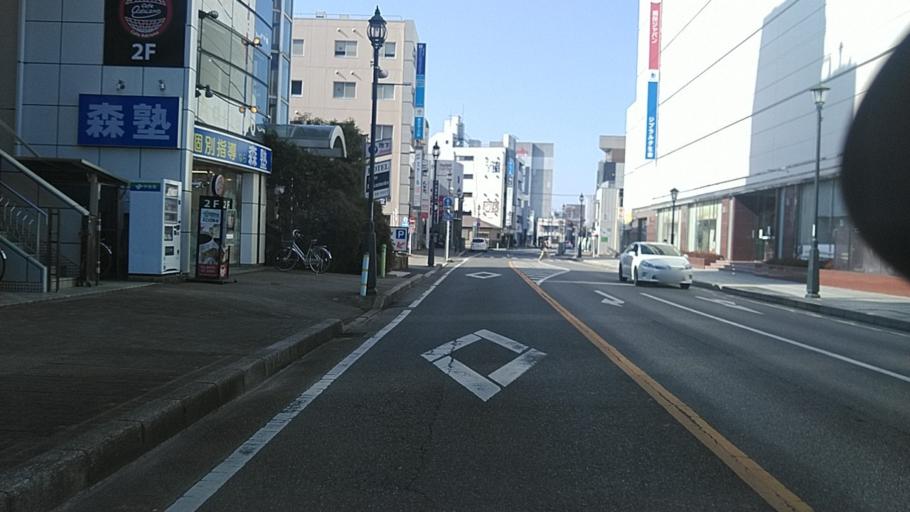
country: JP
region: Chiba
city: Mobara
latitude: 35.4264
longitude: 140.3033
